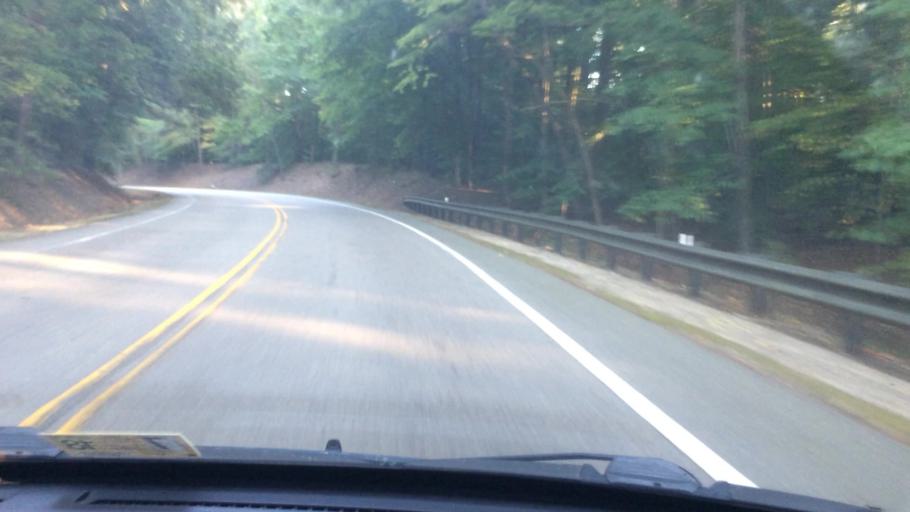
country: US
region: Virginia
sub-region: City of Williamsburg
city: Williamsburg
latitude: 37.2508
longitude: -76.7085
